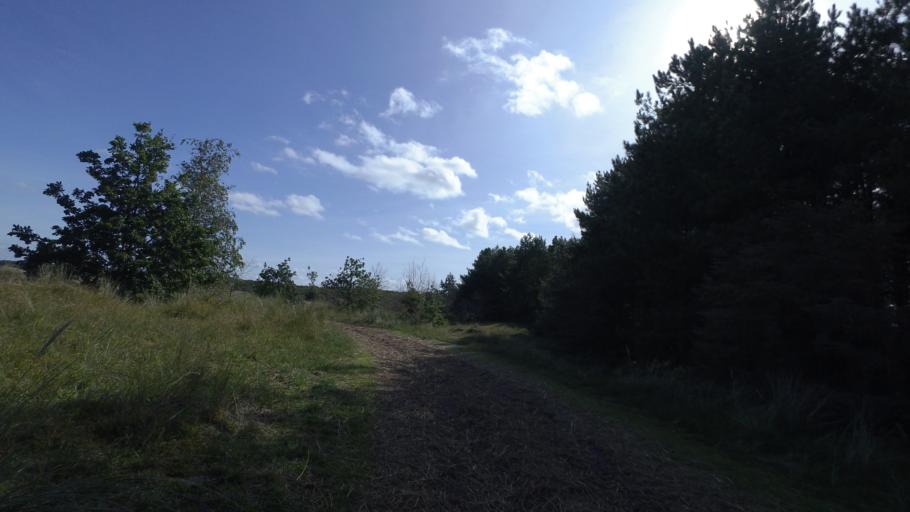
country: NL
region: Friesland
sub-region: Gemeente Ameland
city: Hollum
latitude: 53.4527
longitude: 5.6961
